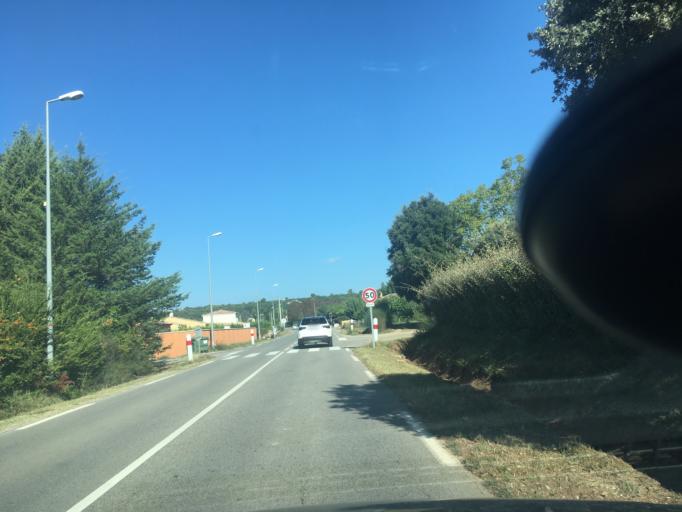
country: FR
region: Provence-Alpes-Cote d'Azur
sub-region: Departement du Var
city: Regusse
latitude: 43.6532
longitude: 6.1453
